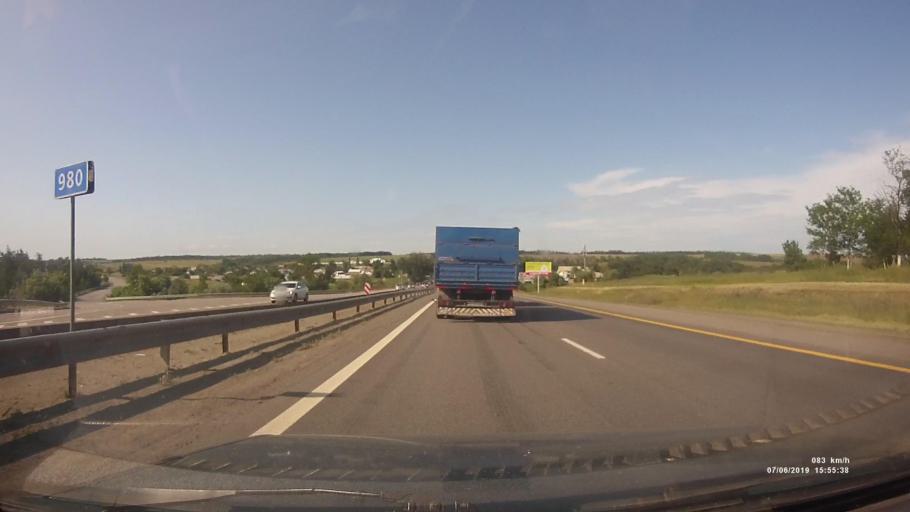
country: RU
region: Rostov
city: Gornyy
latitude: 47.8782
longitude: 40.2094
